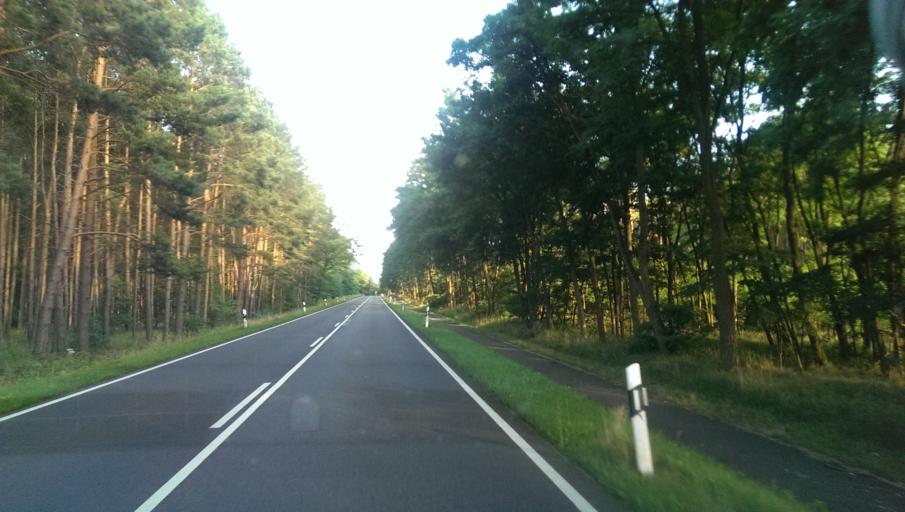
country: DE
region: Brandenburg
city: Treuenbrietzen
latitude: 52.0496
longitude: 12.9131
